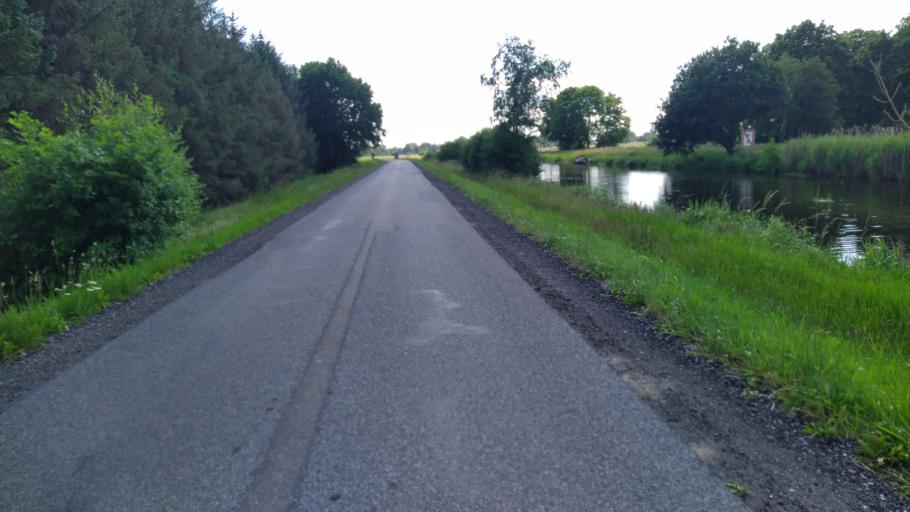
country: DE
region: Lower Saxony
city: Odisheim
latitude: 53.6688
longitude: 8.9131
